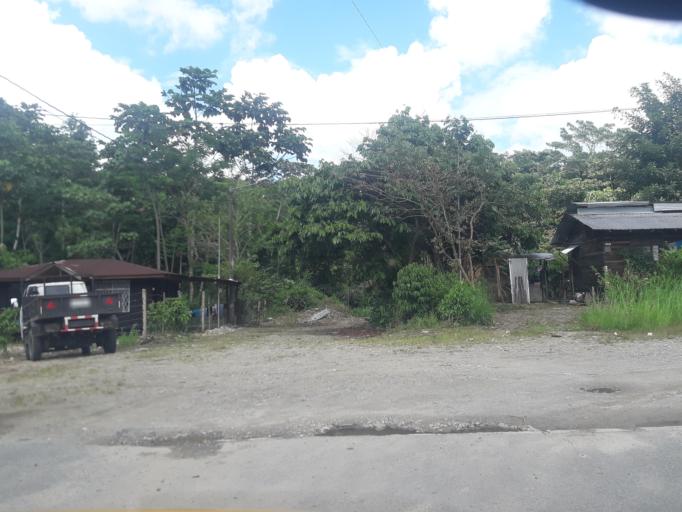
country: EC
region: Napo
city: Tena
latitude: -1.0105
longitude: -77.8124
